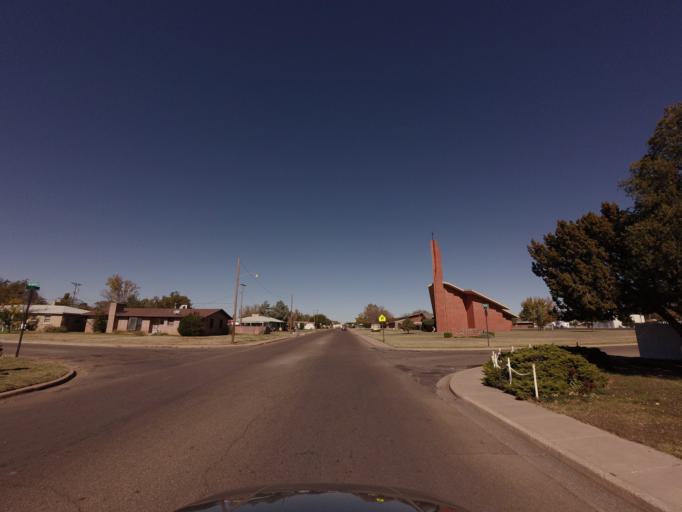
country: US
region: New Mexico
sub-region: Curry County
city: Clovis
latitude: 34.4237
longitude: -103.2069
